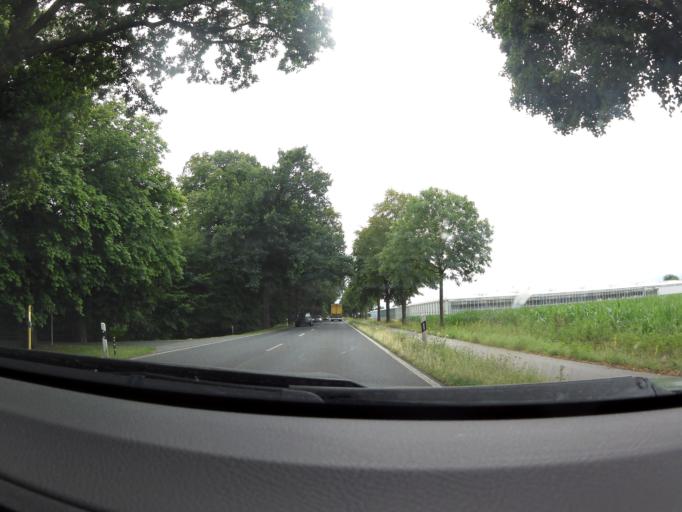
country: DE
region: North Rhine-Westphalia
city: Geldern
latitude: 51.4998
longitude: 6.3027
